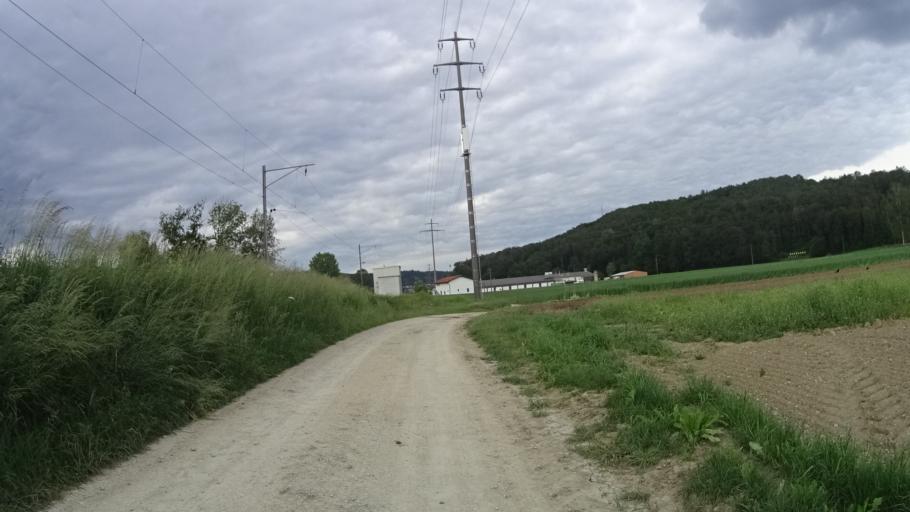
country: CH
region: Aargau
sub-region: Bezirk Zurzach
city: Leibstadt
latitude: 47.6058
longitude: 8.1909
